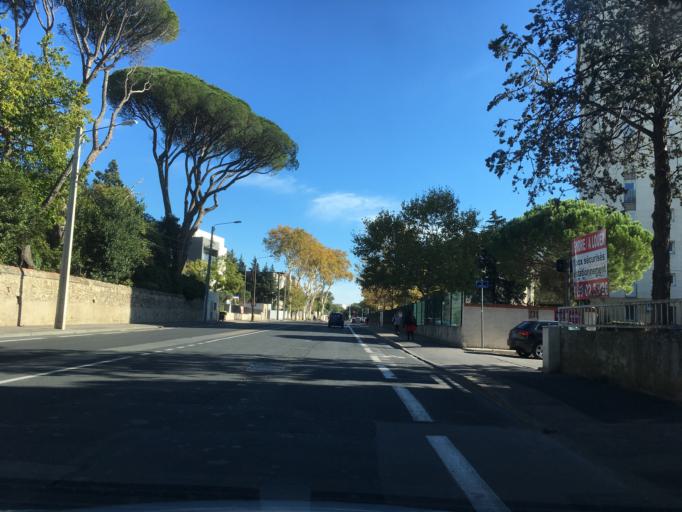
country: FR
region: Languedoc-Roussillon
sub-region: Departement de l'Herault
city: Juvignac
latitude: 43.6144
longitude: 3.8364
